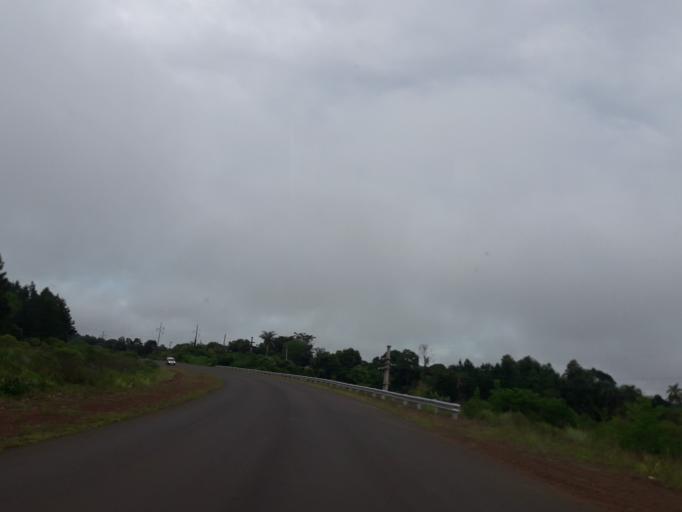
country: AR
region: Misiones
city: Bernardo de Irigoyen
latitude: -26.4211
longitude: -53.8365
